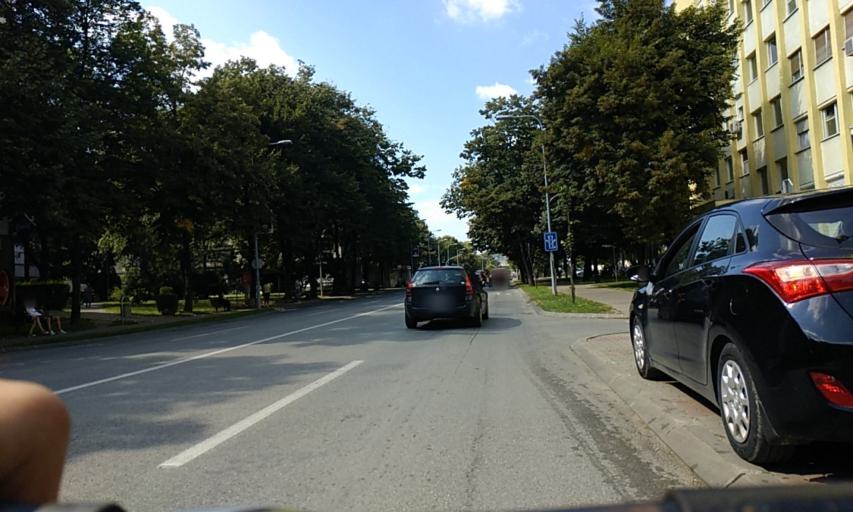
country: BA
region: Republika Srpska
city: Banja Luka
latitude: 44.7694
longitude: 17.1859
